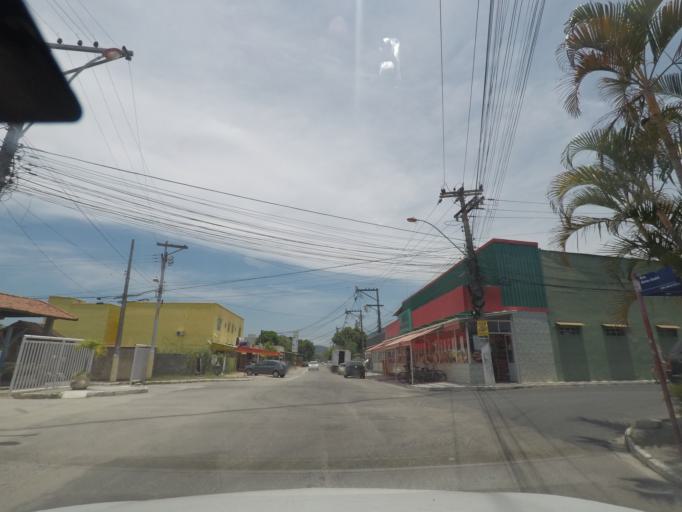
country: BR
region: Rio de Janeiro
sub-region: Marica
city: Marica
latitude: -22.9092
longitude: -42.8317
